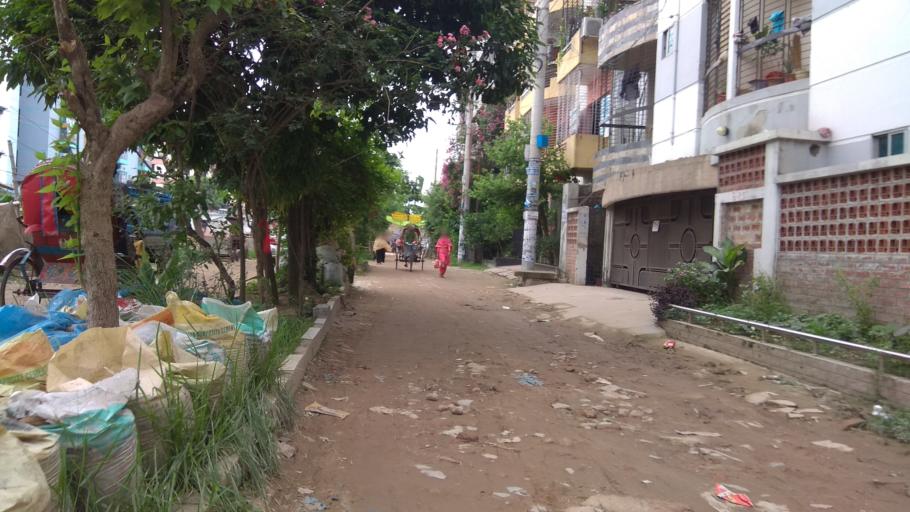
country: BD
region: Dhaka
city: Tungi
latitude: 23.8227
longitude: 90.3533
